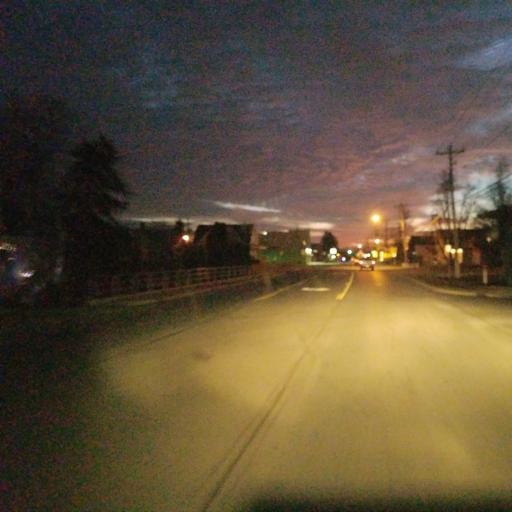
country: US
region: Illinois
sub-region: Peoria County
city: Hanna City
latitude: 40.6923
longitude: -89.7976
